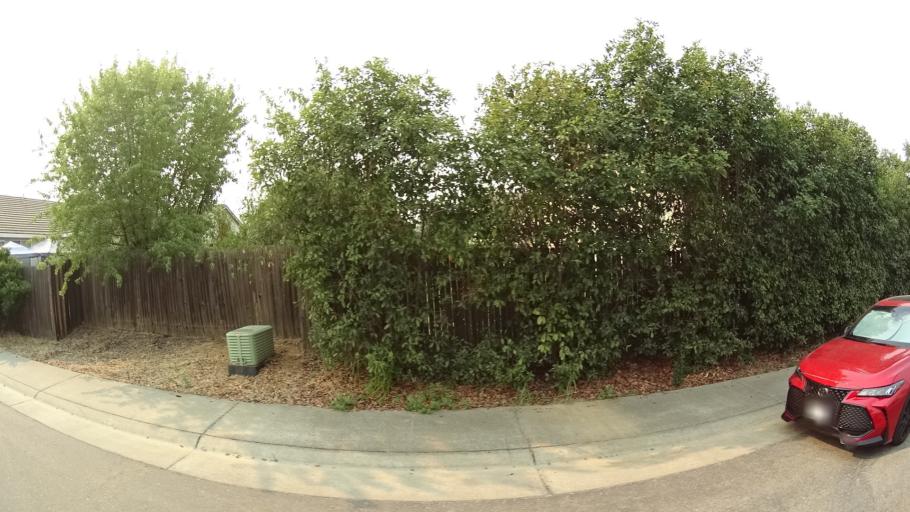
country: US
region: California
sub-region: Sacramento County
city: Laguna
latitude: 38.4021
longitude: -121.4465
